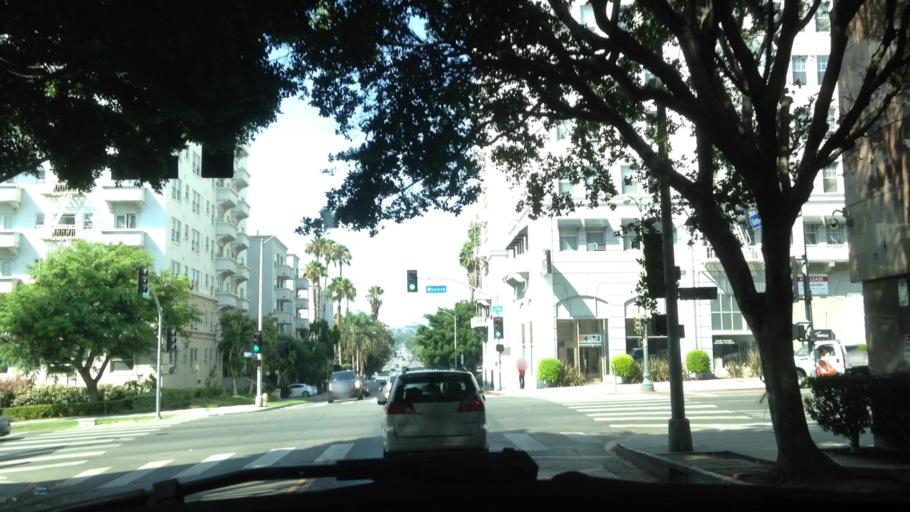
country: US
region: California
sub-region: Los Angeles County
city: Echo Park
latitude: 34.0606
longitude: -118.2826
